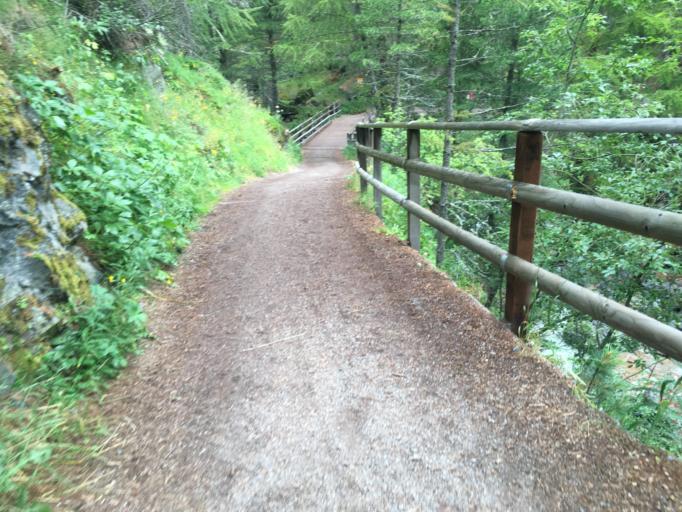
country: CH
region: Valais
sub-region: Visp District
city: Zermatt
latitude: 46.0089
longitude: 7.7329
